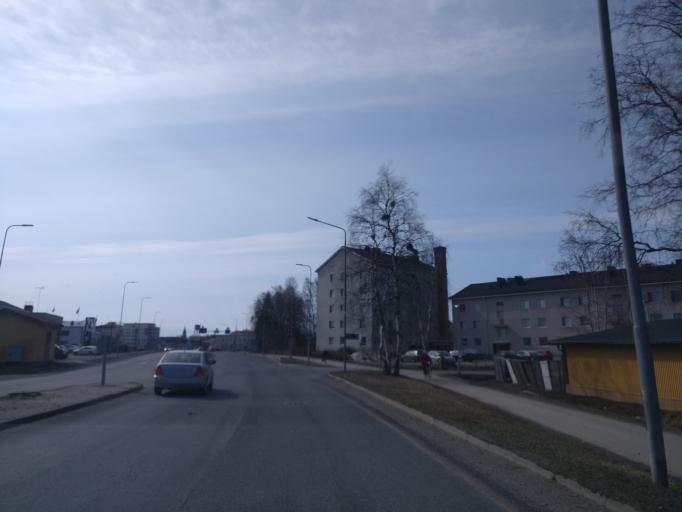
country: FI
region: Lapland
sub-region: Kemi-Tornio
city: Kemi
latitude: 65.7425
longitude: 24.5658
